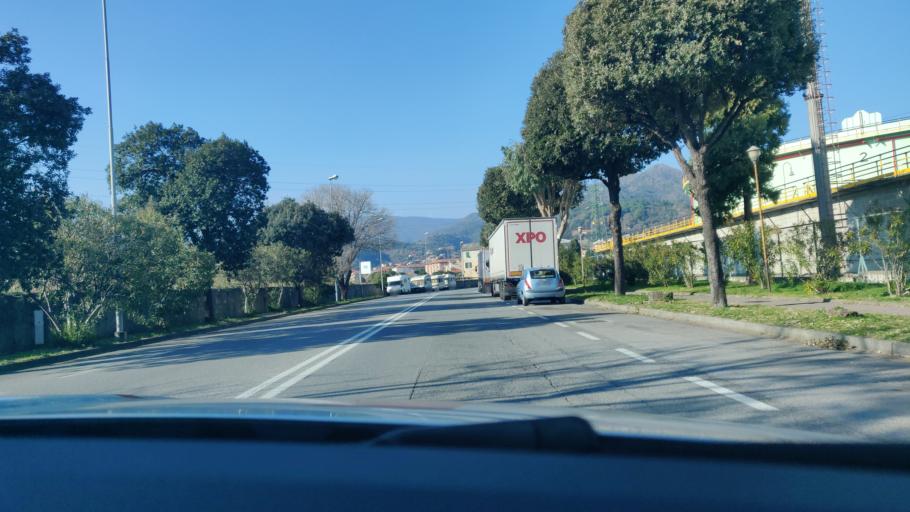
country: IT
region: Liguria
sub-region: Provincia di Savona
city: Quiliano
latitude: 44.2900
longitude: 8.4215
